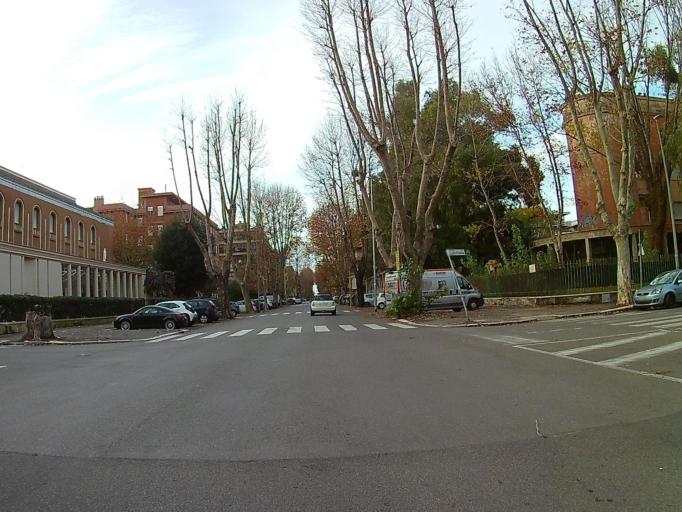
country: IT
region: Latium
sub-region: Citta metropolitana di Roma Capitale
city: Lido di Ostia
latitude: 41.7338
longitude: 12.2718
